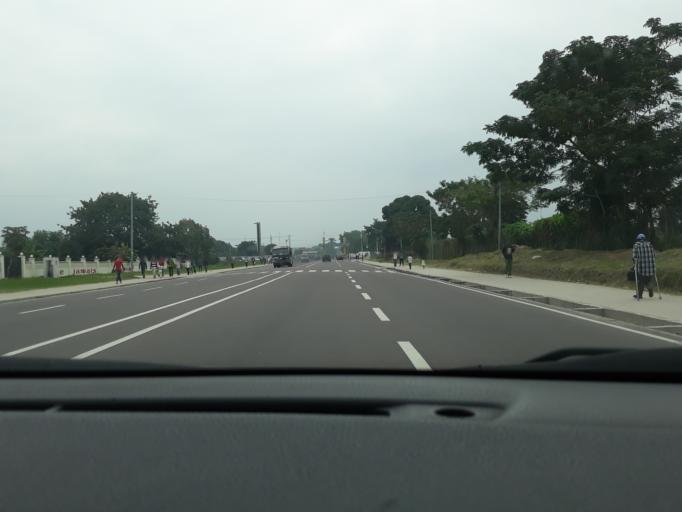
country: CD
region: Kinshasa
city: Kinshasa
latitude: -4.3312
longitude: 15.2989
